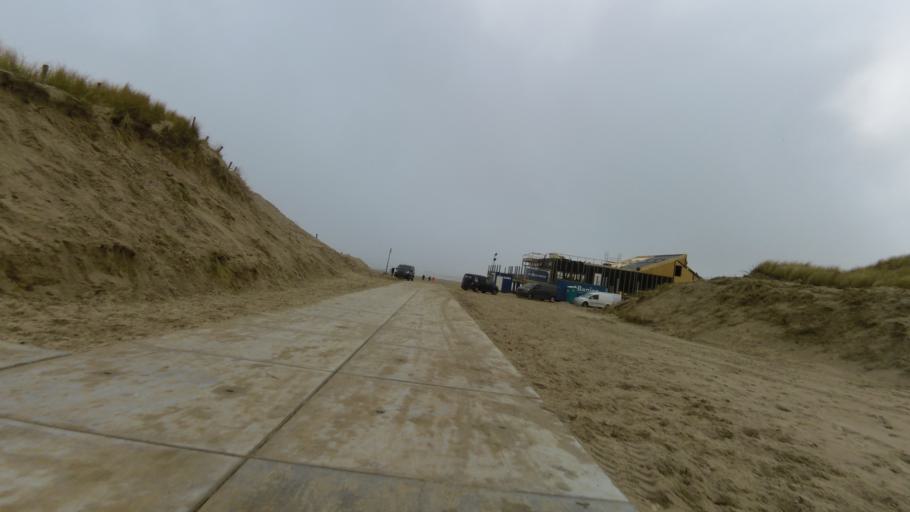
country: NL
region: North Holland
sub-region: Gemeente Bergen
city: Egmond aan Zee
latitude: 52.7144
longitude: 4.6401
